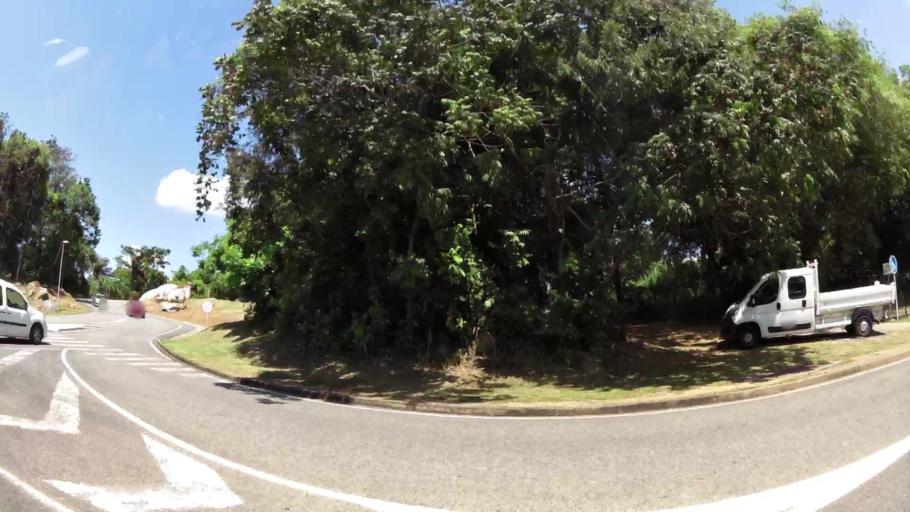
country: GF
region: Guyane
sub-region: Guyane
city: Cayenne
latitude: 4.9193
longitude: -52.3218
